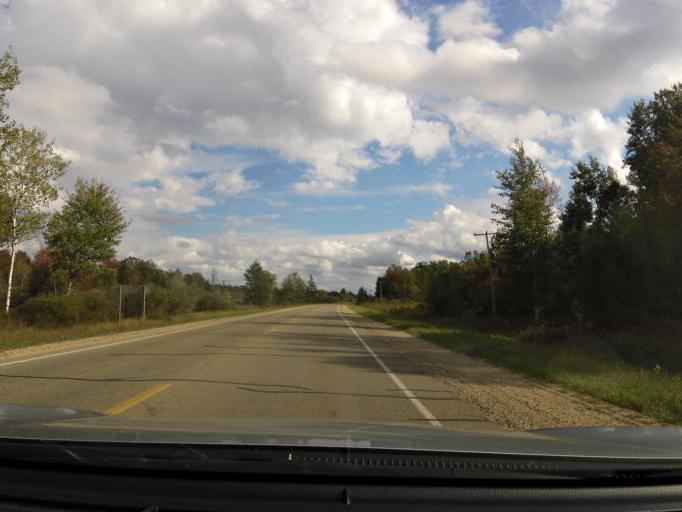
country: US
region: Michigan
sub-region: Roscommon County
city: Saint Helen
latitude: 44.4059
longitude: -84.4498
